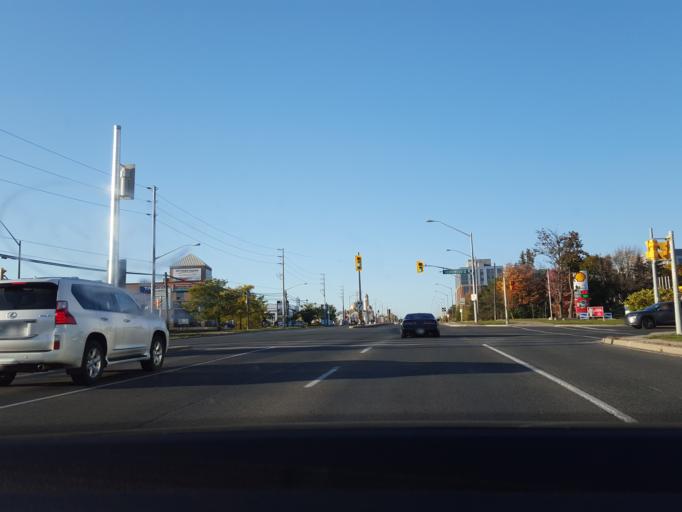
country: CA
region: Ontario
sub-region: York
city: Richmond Hill
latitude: 43.8982
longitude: -79.4434
